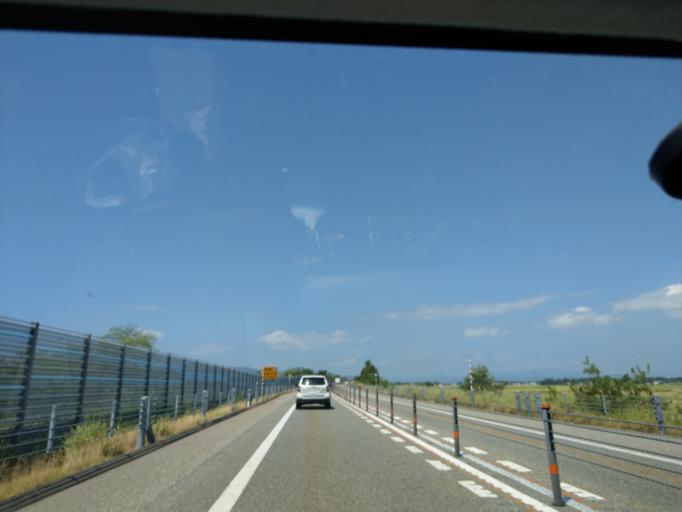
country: JP
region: Akita
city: Omagari
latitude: 39.3787
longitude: 140.4811
